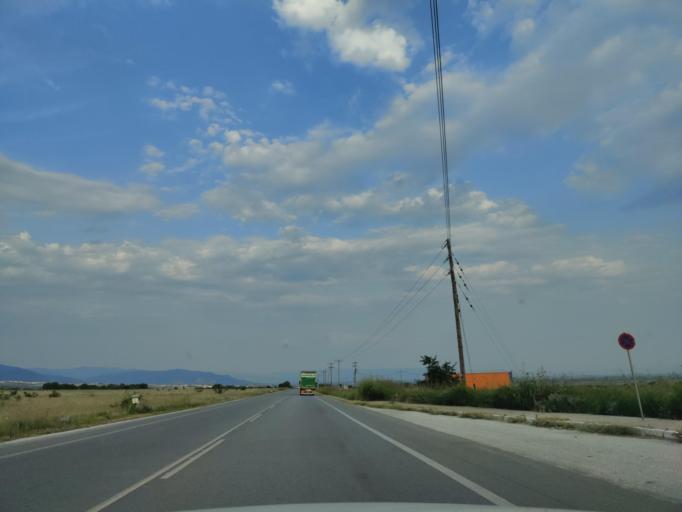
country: GR
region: East Macedonia and Thrace
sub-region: Nomos Dramas
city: Petroussa
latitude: 41.1754
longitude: 24.0118
